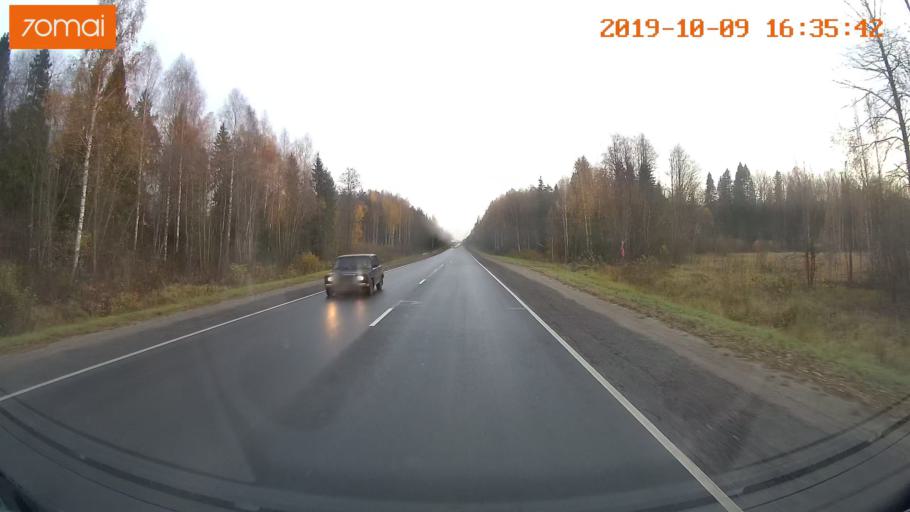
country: RU
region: Kostroma
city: Volgorechensk
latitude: 57.5520
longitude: 41.0039
